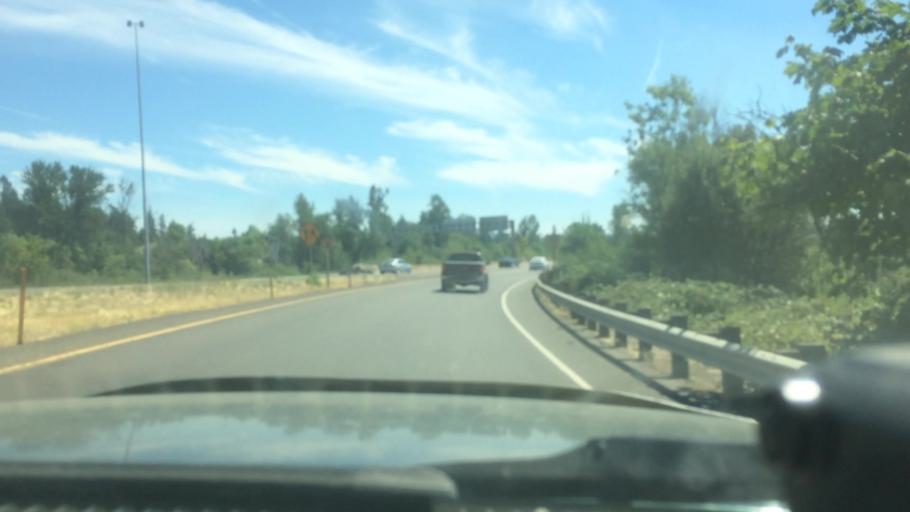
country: US
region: Oregon
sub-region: Lane County
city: Eugene
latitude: 44.0899
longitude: -123.1005
